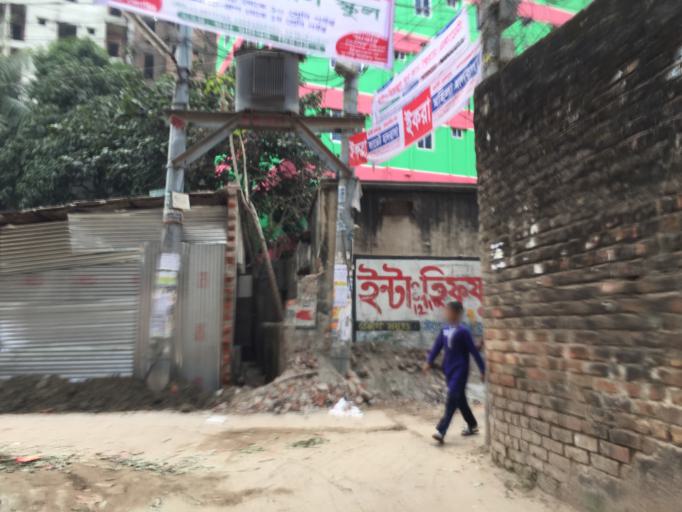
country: BD
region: Dhaka
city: Azimpur
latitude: 23.7978
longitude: 90.3634
